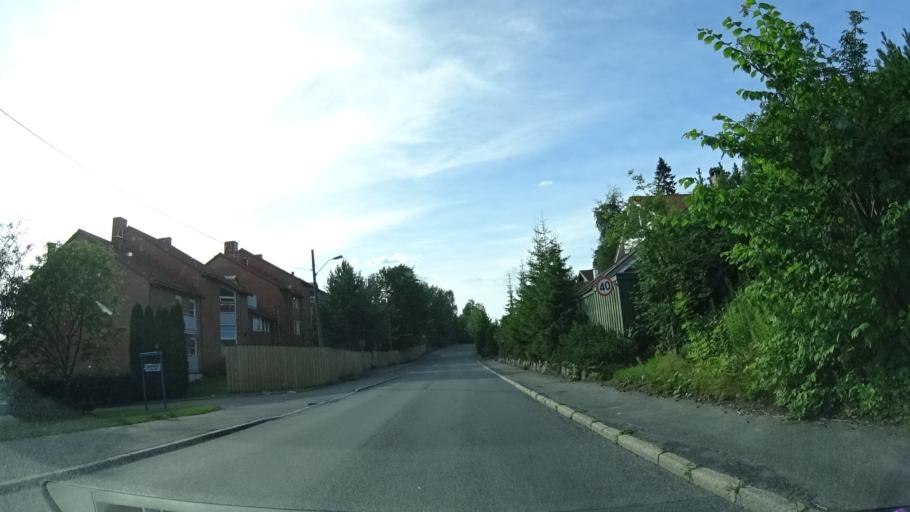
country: NO
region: Oslo
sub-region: Oslo
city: Sjolyststranda
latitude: 59.9563
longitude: 10.6552
